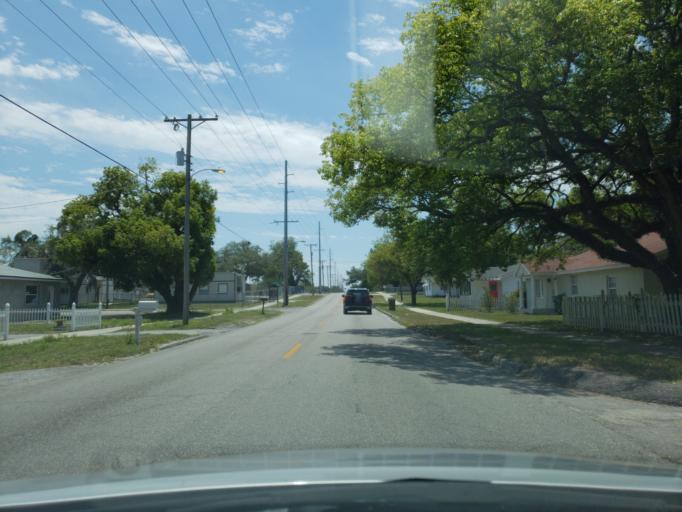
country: US
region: Florida
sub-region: Hillsborough County
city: Carrollwood
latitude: 28.0429
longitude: -82.4677
